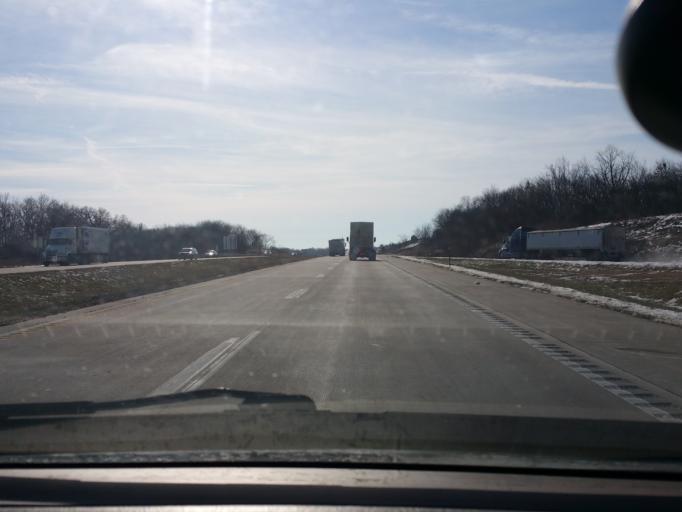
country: US
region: Missouri
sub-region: Clinton County
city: Cameron
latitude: 39.6664
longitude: -94.2362
